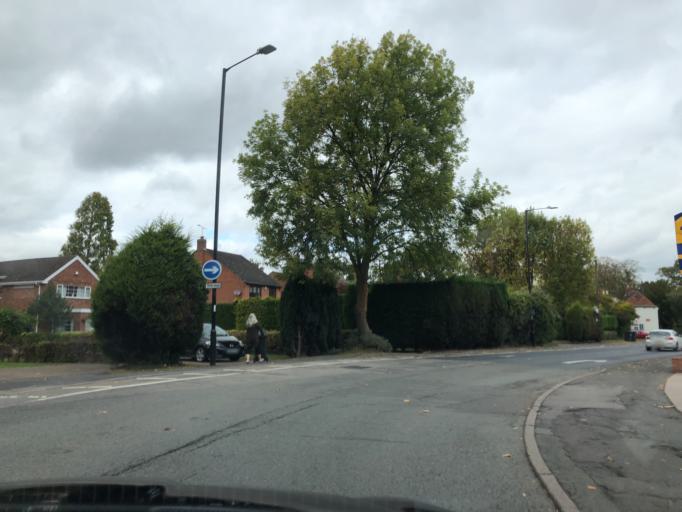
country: GB
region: England
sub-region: Warwickshire
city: Kenilworth
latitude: 52.3357
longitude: -1.5729
